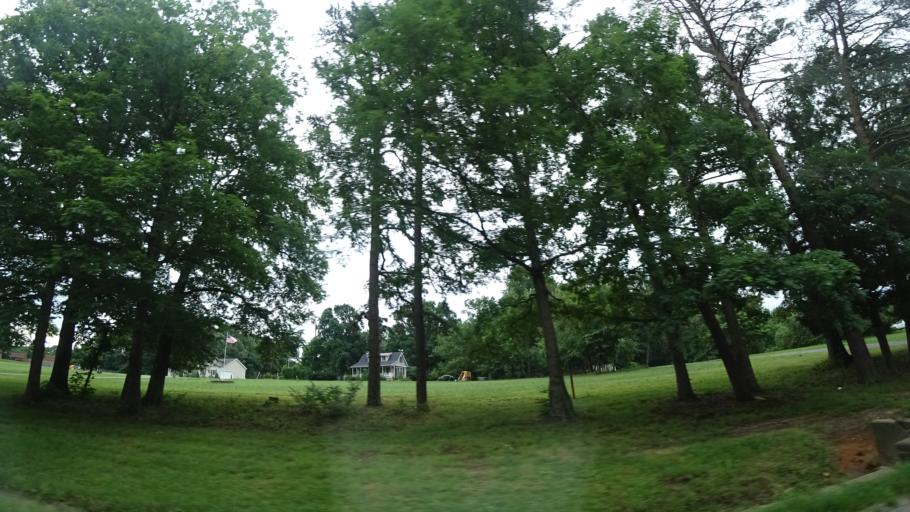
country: US
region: Virginia
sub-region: Spotsylvania County
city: Spotsylvania Courthouse
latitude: 38.1232
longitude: -77.7406
